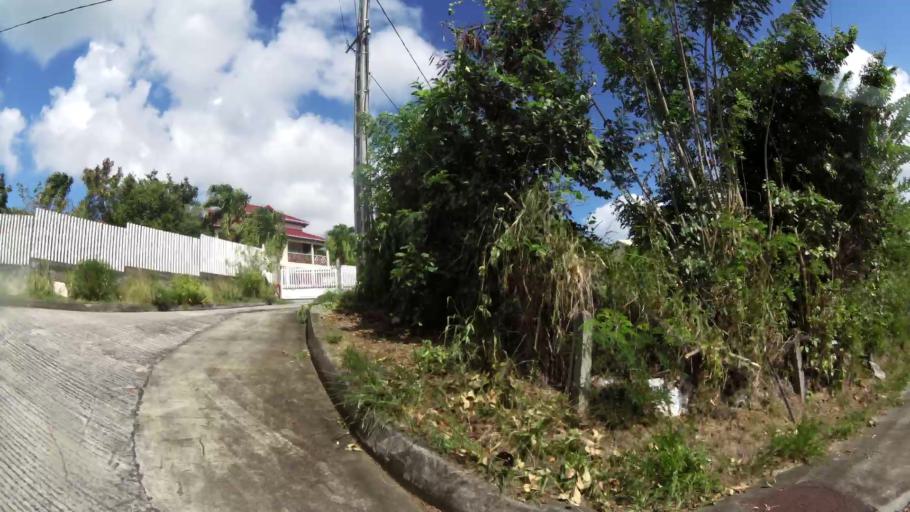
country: MQ
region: Martinique
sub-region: Martinique
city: Fort-de-France
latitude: 14.6337
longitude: -61.1287
